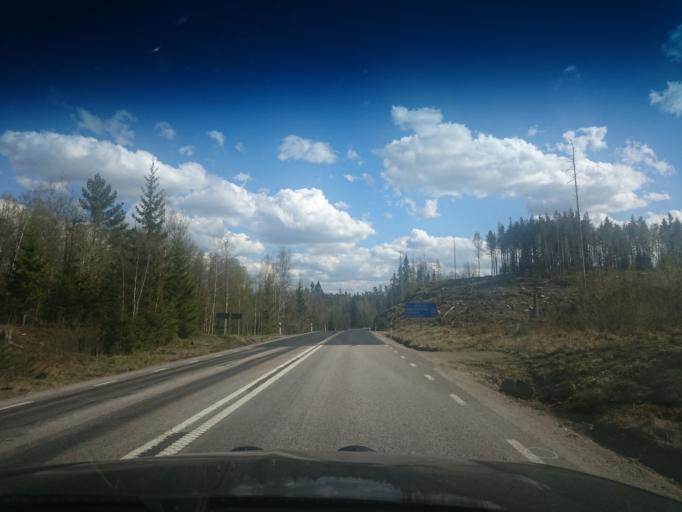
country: SE
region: Joenkoeping
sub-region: Vetlanda Kommun
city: Vetlanda
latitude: 57.2915
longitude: 15.1296
